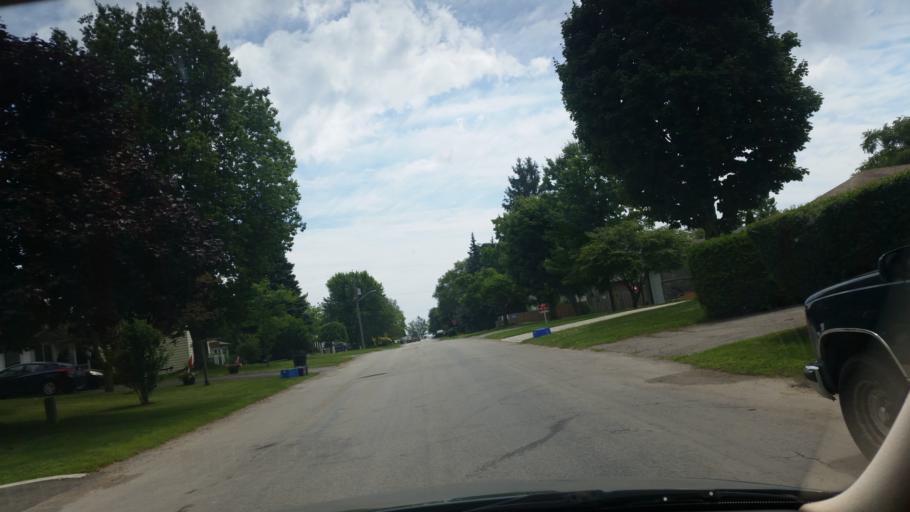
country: CA
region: Ontario
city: Norfolk County
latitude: 42.7909
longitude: -80.1807
